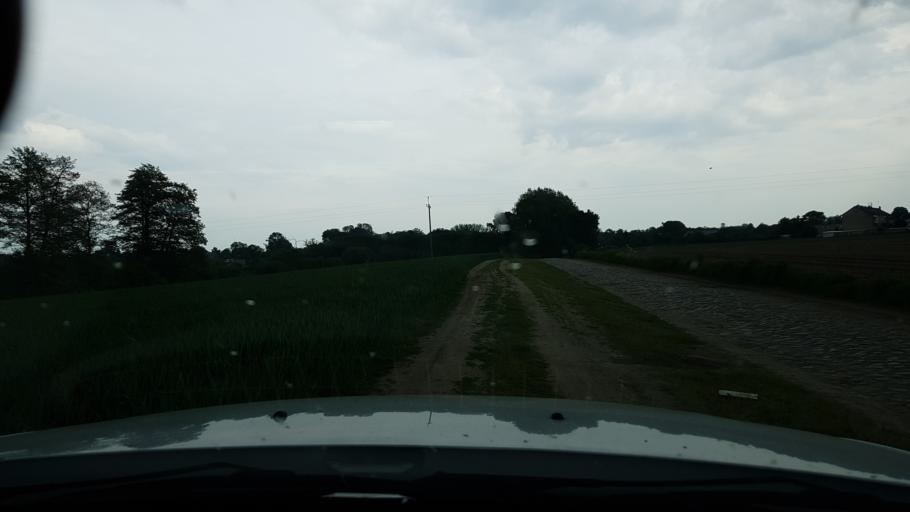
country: PL
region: West Pomeranian Voivodeship
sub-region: Powiat stargardzki
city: Stara Dabrowa
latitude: 53.3446
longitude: 15.1859
